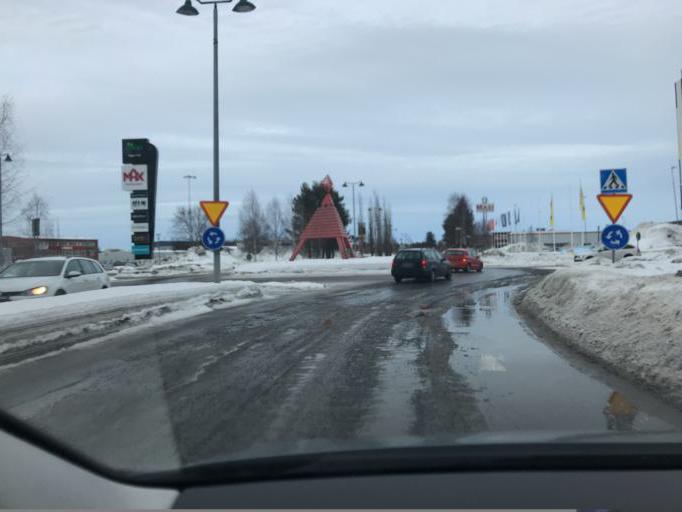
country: SE
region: Norrbotten
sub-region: Lulea Kommun
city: Gammelstad
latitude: 65.6171
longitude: 22.0423
